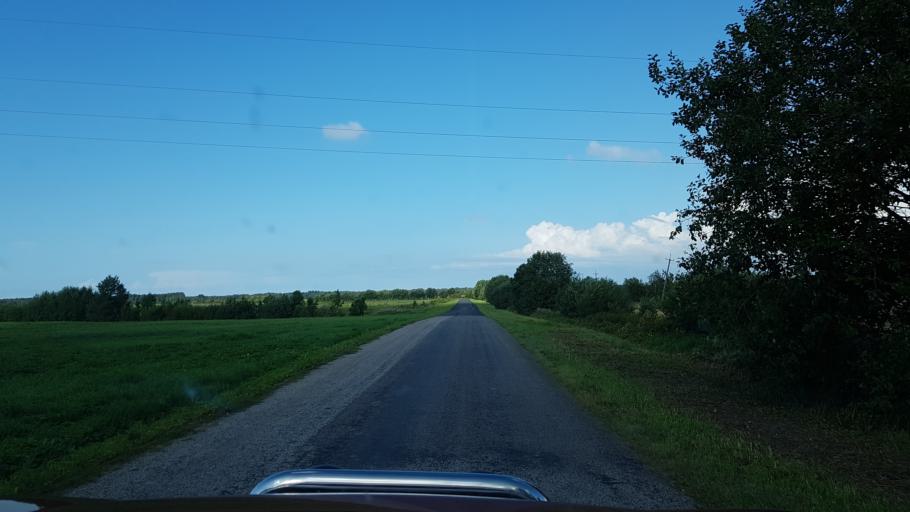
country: EE
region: Harju
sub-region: Paldiski linn
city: Paldiski
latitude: 59.2386
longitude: 24.0205
